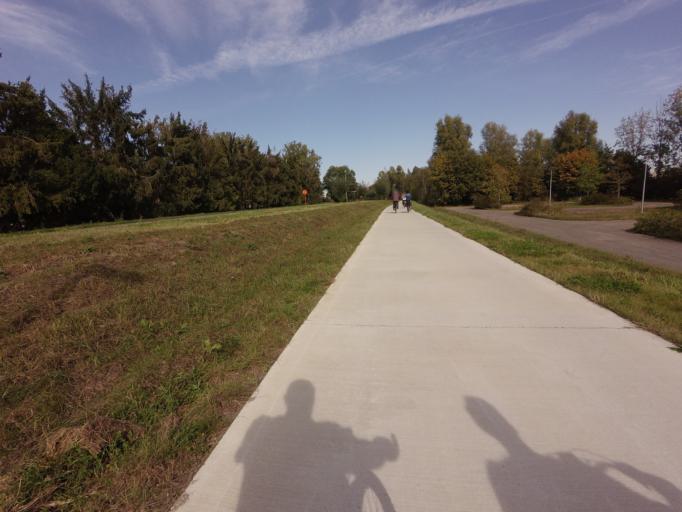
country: BE
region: Flanders
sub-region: Provincie Limburg
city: Maaseik
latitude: 51.1329
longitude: 5.8158
